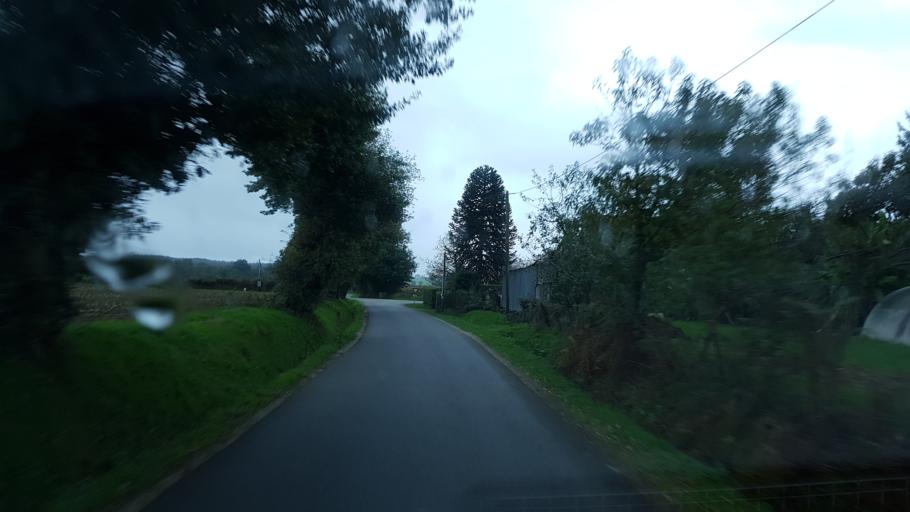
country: FR
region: Brittany
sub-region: Departement du Morbihan
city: Elven
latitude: 47.7338
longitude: -2.5748
